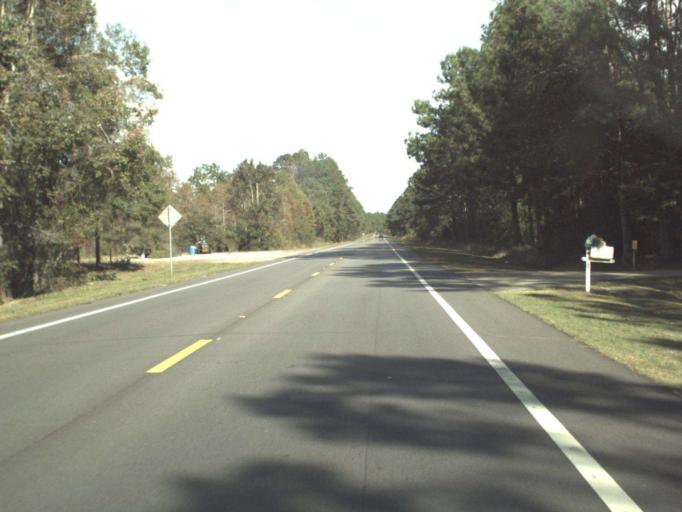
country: US
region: Florida
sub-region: Holmes County
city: Bonifay
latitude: 30.7780
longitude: -85.8001
